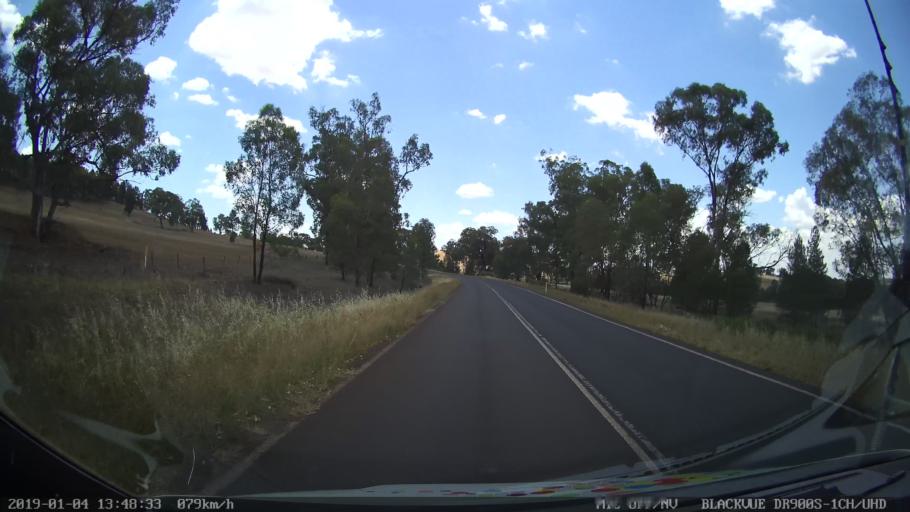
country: AU
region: New South Wales
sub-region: Dubbo Municipality
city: Dubbo
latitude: -32.4413
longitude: 148.5844
